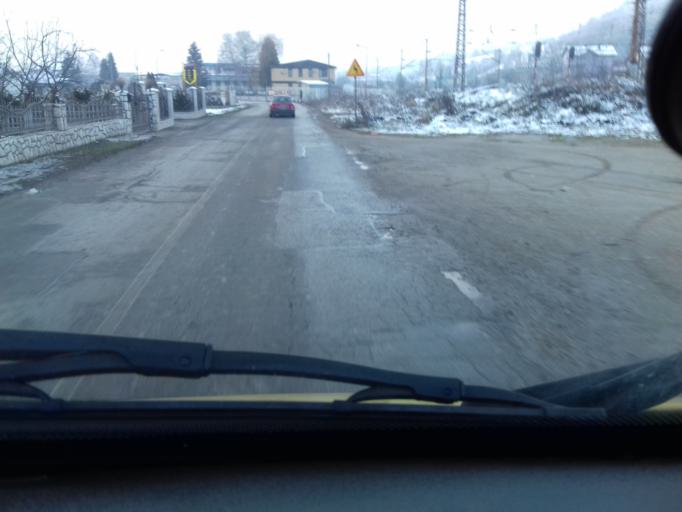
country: BA
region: Federation of Bosnia and Herzegovina
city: Visoko
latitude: 43.9983
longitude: 18.1807
